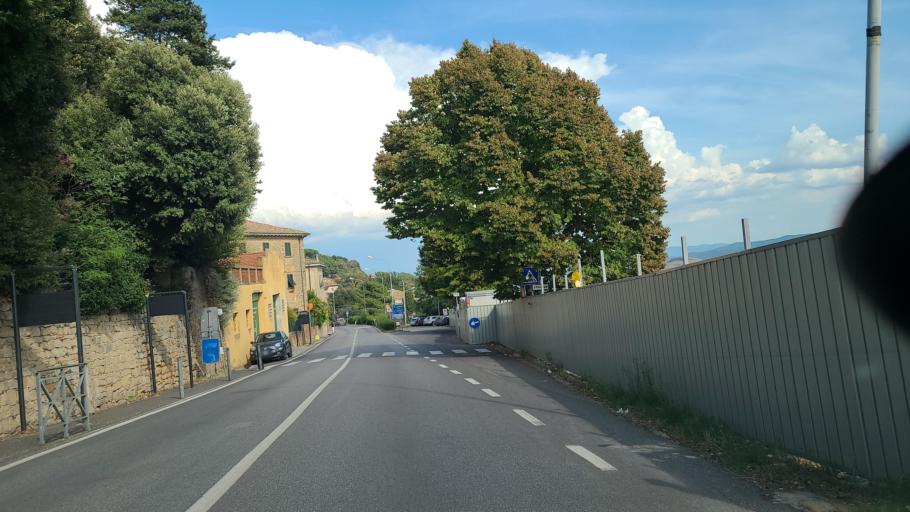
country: IT
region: Tuscany
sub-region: Province of Pisa
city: Volterra
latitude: 43.3993
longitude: 10.8660
